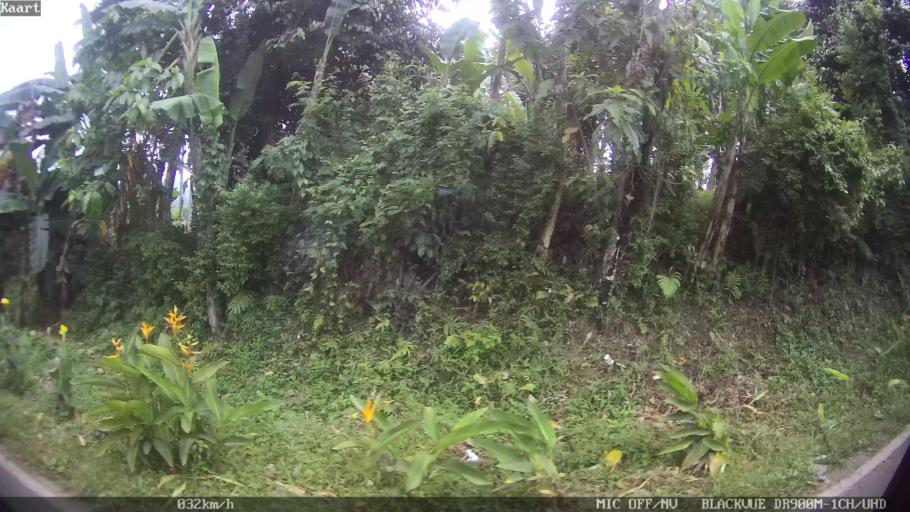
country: ID
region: Lampung
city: Bandarlampung
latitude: -5.4383
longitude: 105.2380
